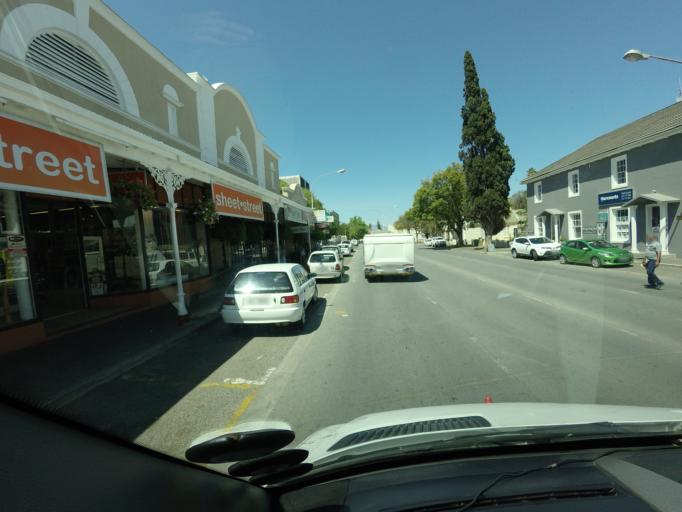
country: ZA
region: Western Cape
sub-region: Eden District Municipality
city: Oudtshoorn
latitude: -33.5890
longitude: 22.2033
